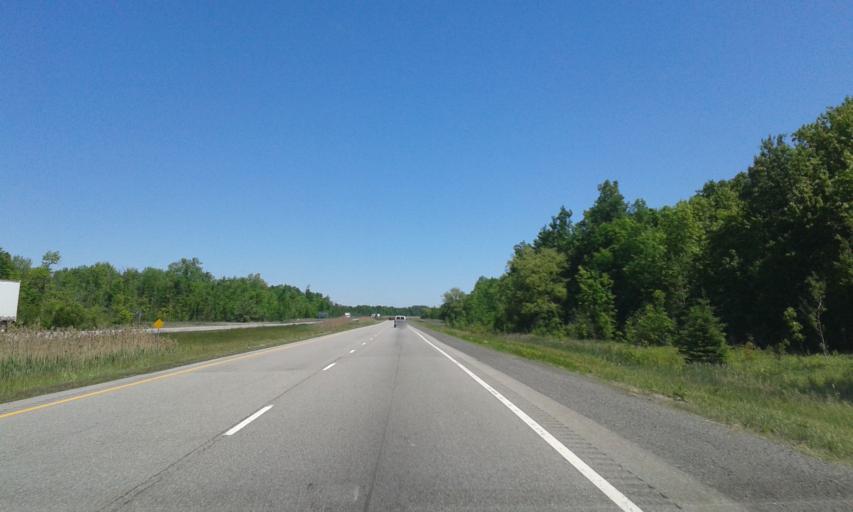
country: CA
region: Ontario
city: Prescott
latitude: 44.7649
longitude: -75.4651
